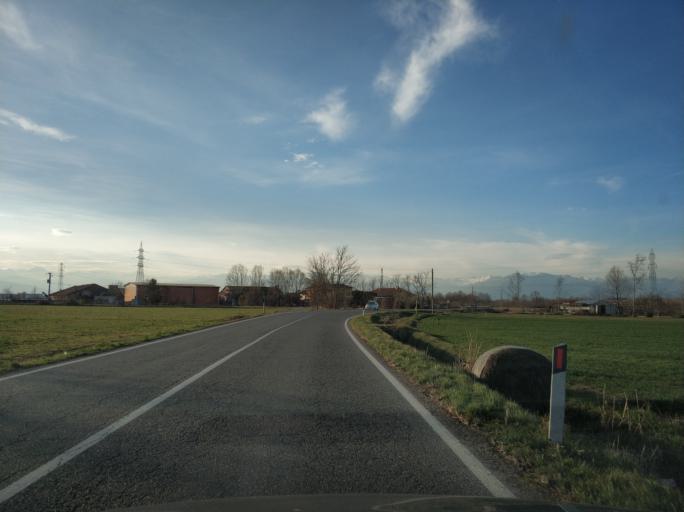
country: IT
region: Piedmont
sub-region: Provincia di Torino
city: Brandizzo
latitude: 45.1853
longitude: 7.8265
